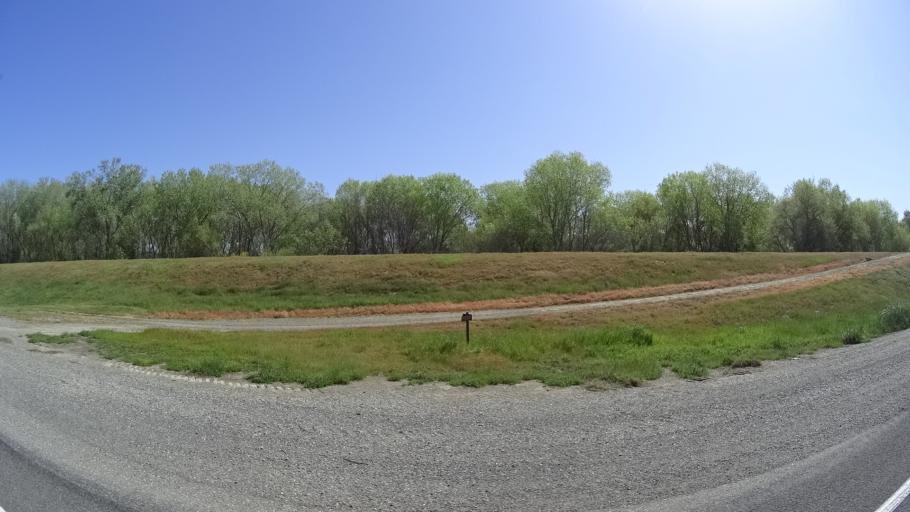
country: US
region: California
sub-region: Glenn County
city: Willows
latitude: 39.4351
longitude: -122.0110
